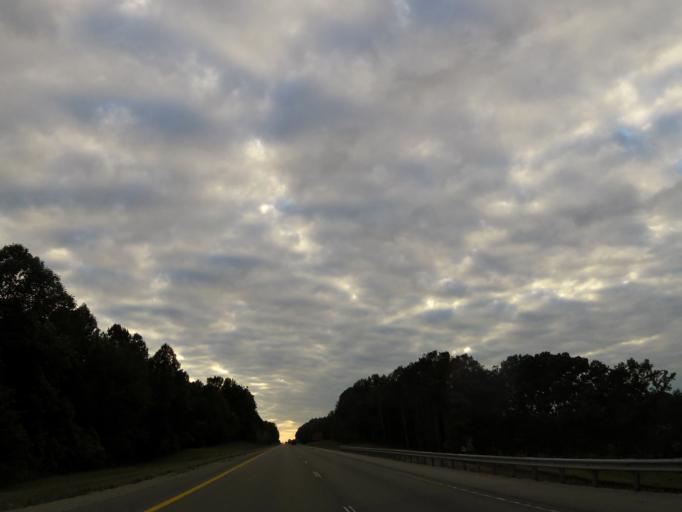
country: US
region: Tennessee
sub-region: Putnam County
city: Baxter
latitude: 36.1403
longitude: -85.5852
